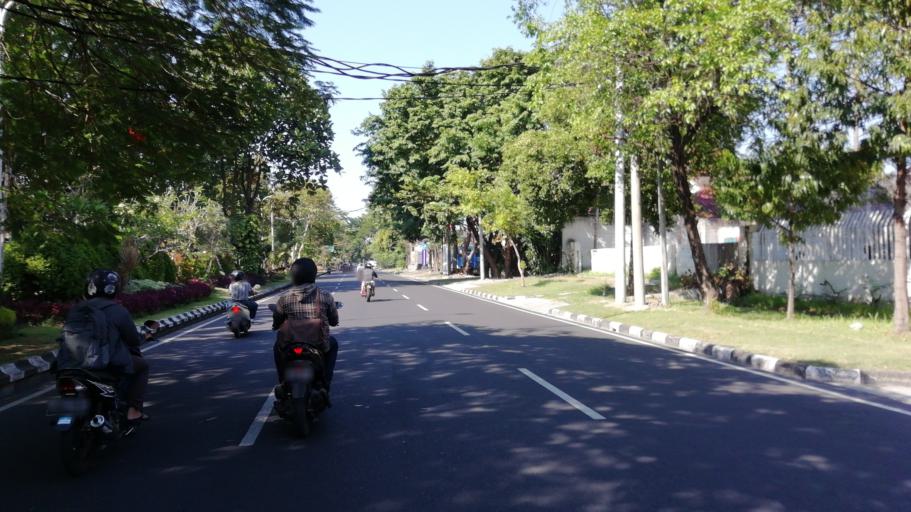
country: ID
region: Bali
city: Banjar Batanpoh
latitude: -8.6711
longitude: 115.2384
